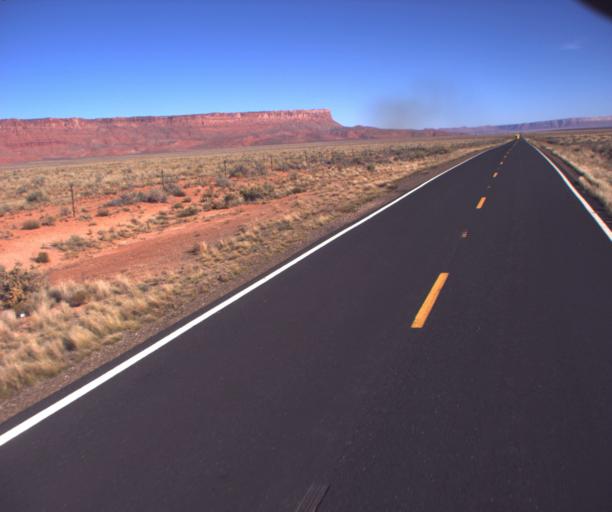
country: US
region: Arizona
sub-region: Coconino County
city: Page
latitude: 36.7086
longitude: -111.9629
